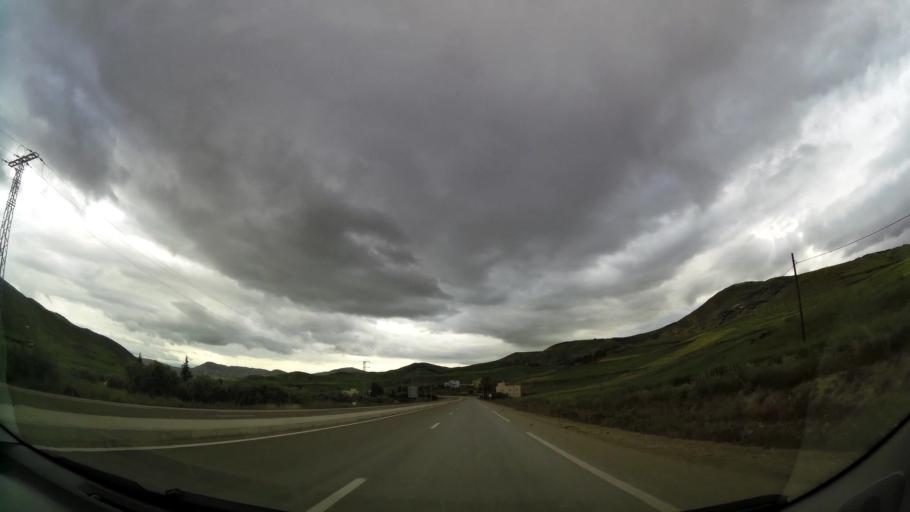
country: MA
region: Taza-Al Hoceima-Taounate
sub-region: Taza
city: Taza
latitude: 34.3406
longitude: -3.9328
